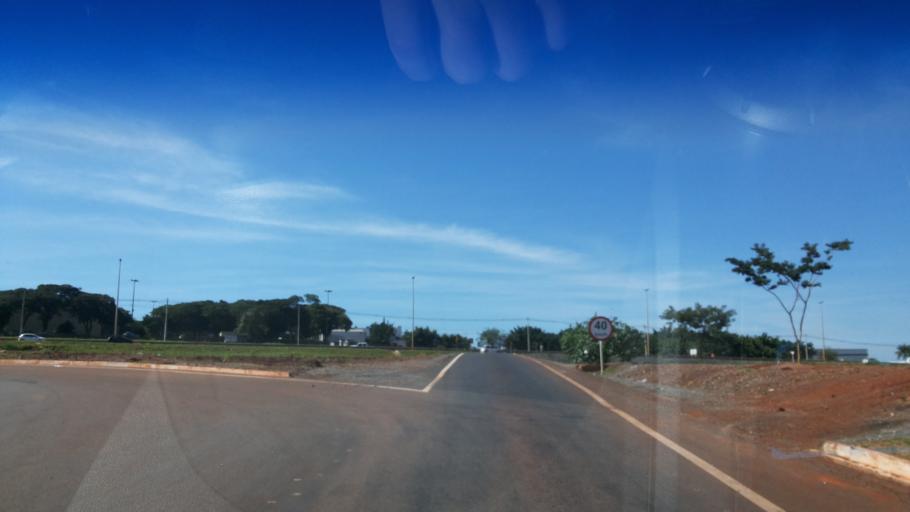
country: BR
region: Goias
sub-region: Goiania
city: Goiania
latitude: -16.6280
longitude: -49.2069
